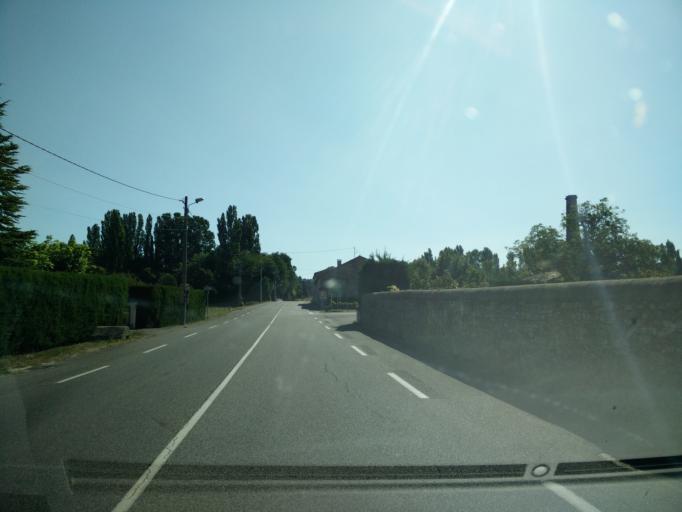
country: FR
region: Rhone-Alpes
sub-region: Departement de la Drome
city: Dieulefit
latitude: 44.5296
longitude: 5.0190
